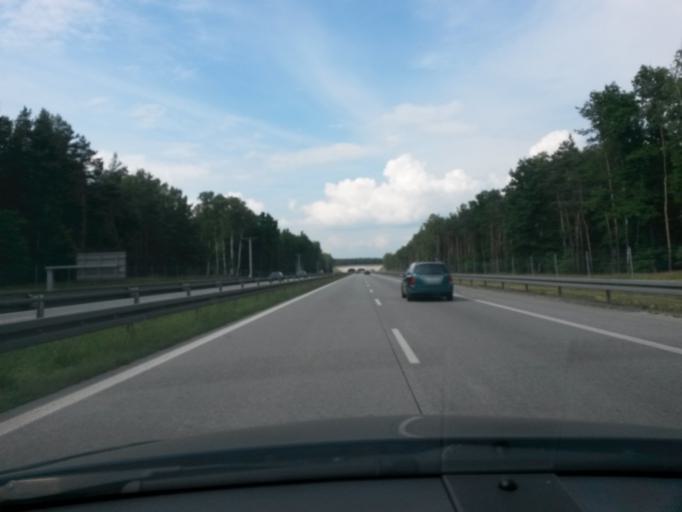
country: PL
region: Lodz Voivodeship
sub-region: Powiat tomaszowski
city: Tomaszow Mazowiecki
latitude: 51.5717
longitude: 20.0262
